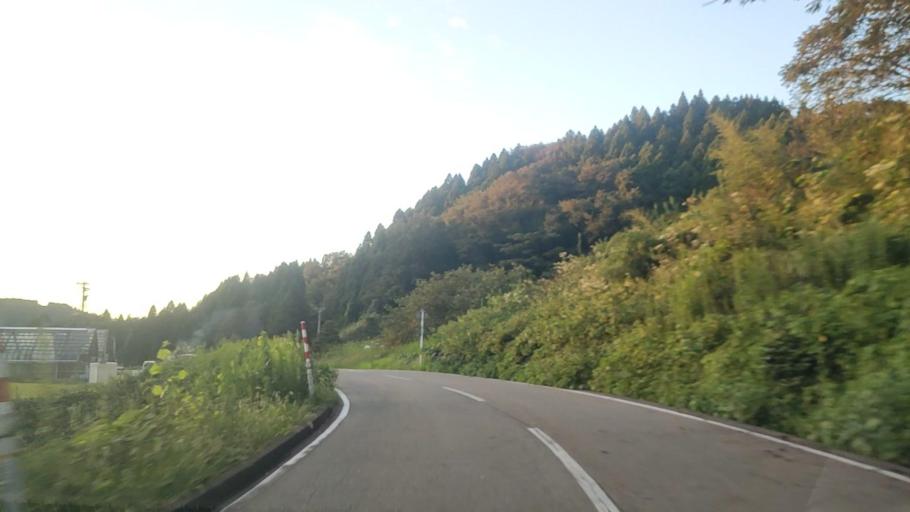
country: JP
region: Ishikawa
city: Tsubata
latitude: 36.6257
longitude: 136.7787
